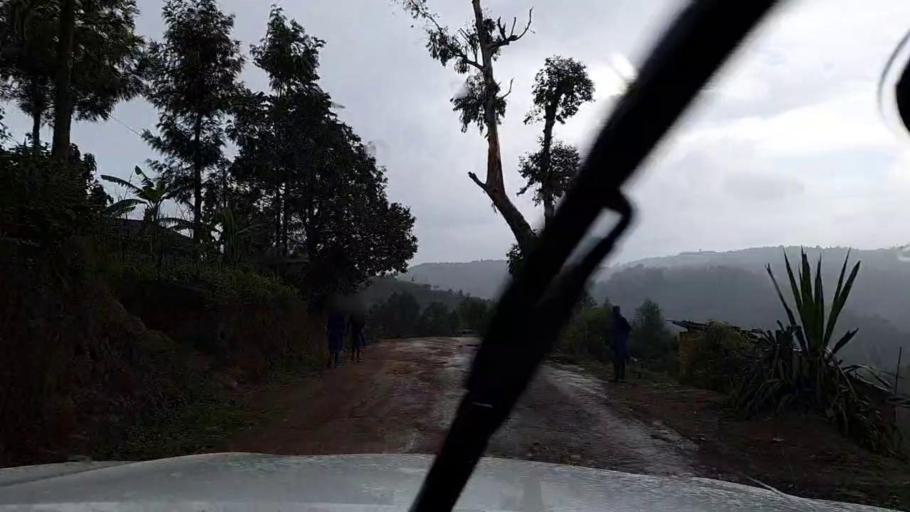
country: BI
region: Kayanza
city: Kayanza
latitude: -2.7761
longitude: 29.5371
